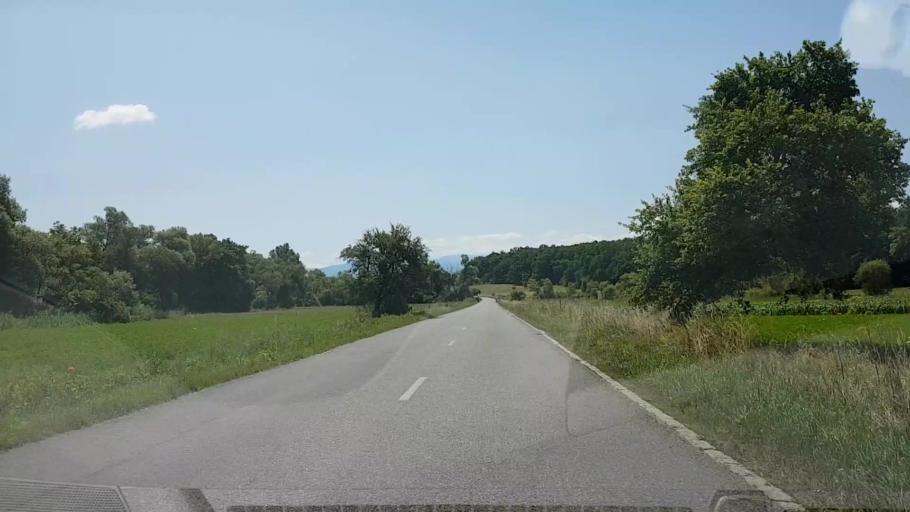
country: RO
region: Brasov
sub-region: Comuna Cincu
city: Cincu
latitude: 45.8748
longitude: 24.8192
